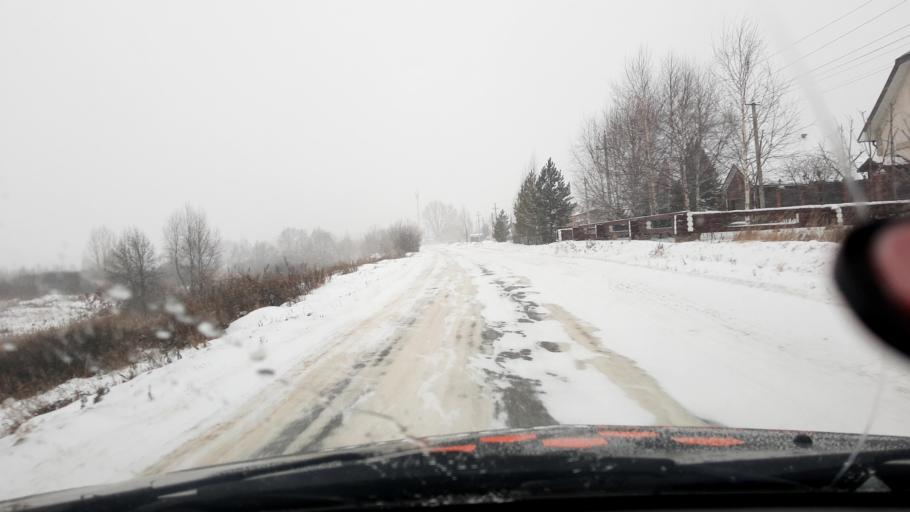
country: RU
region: Bashkortostan
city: Ufa
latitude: 54.5466
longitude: 55.9449
